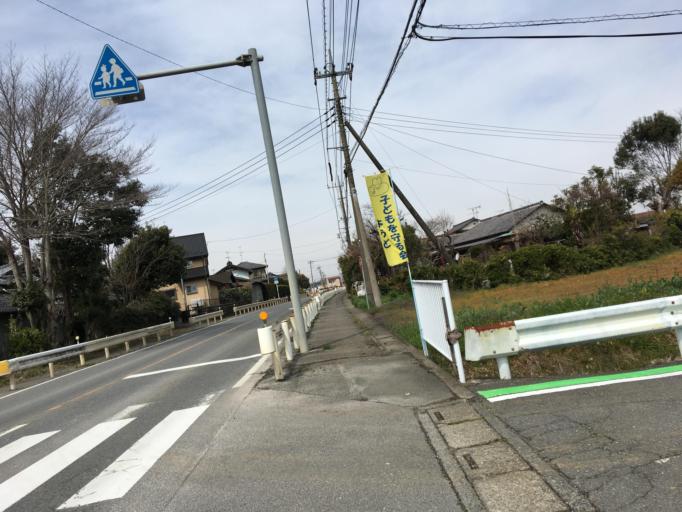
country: JP
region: Saitama
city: Yorii
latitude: 36.1486
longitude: 139.2051
